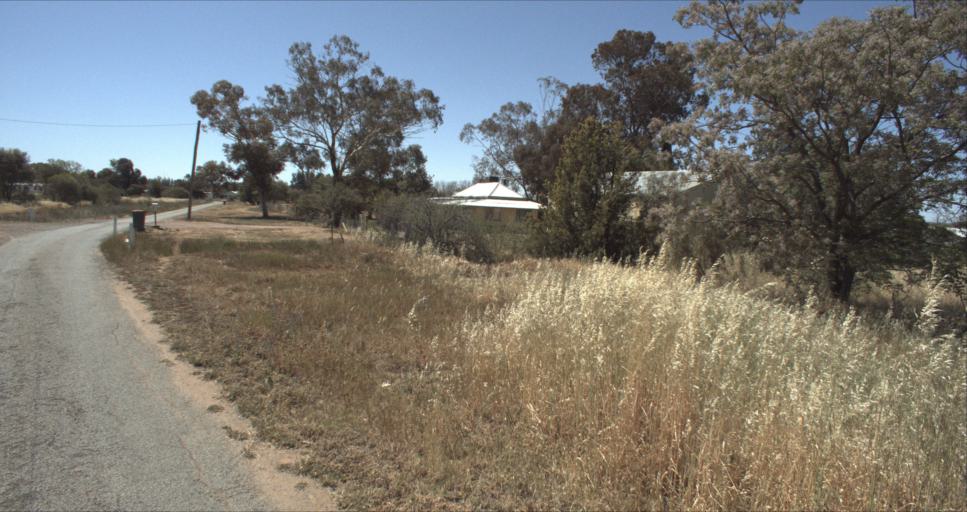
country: AU
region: New South Wales
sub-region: Leeton
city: Leeton
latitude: -34.5284
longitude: 146.3331
